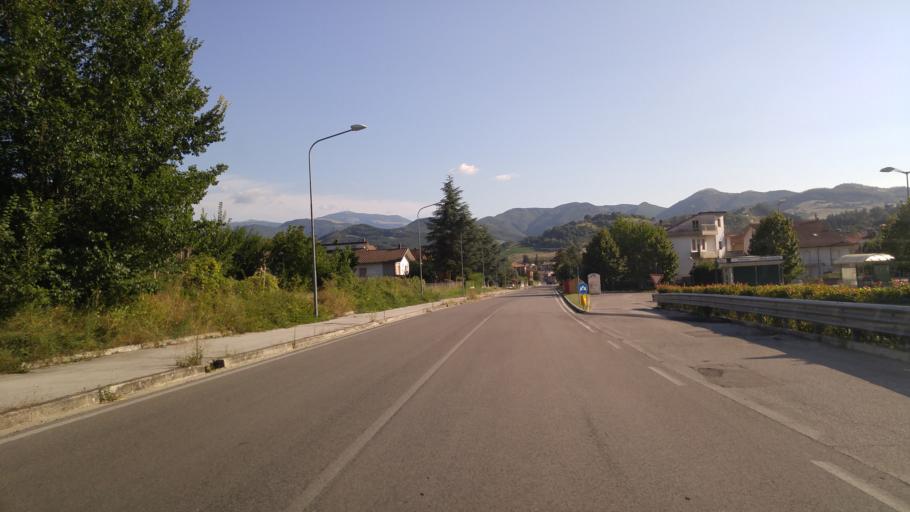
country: IT
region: The Marches
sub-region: Provincia di Pesaro e Urbino
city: Urbania
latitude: 43.6747
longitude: 12.5241
